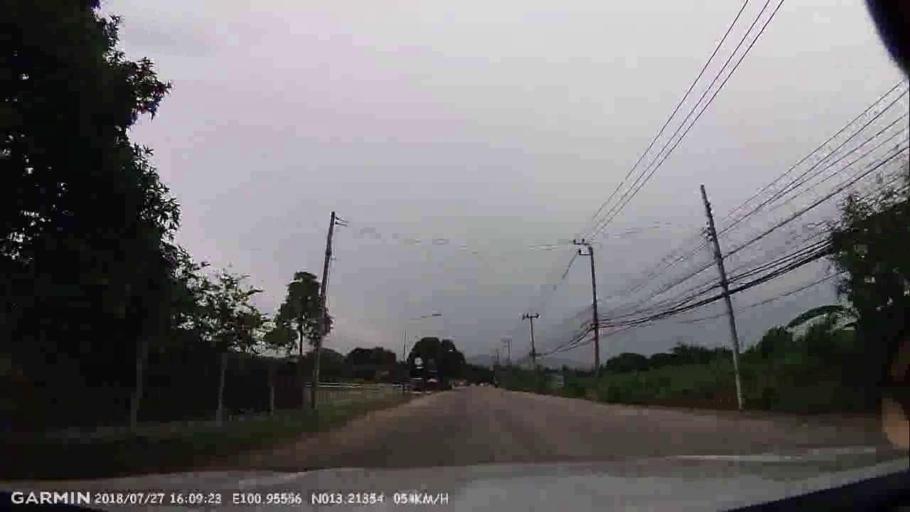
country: TH
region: Chon Buri
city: Si Racha
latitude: 13.2136
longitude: 100.9556
